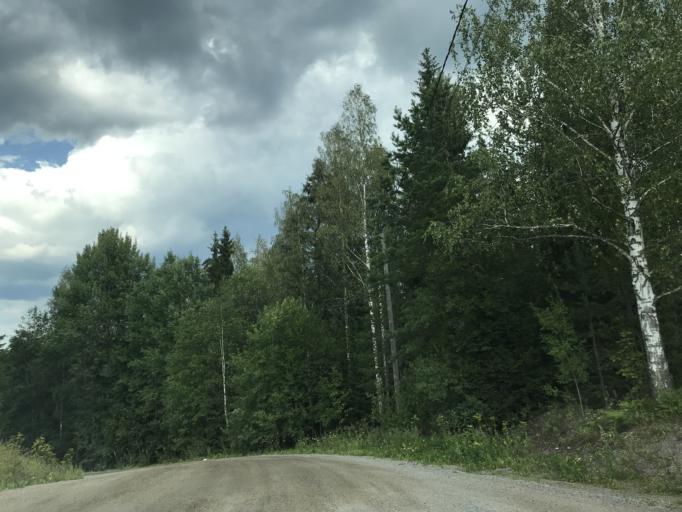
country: FI
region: Uusimaa
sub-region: Helsinki
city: Vihti
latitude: 60.3885
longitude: 24.3335
